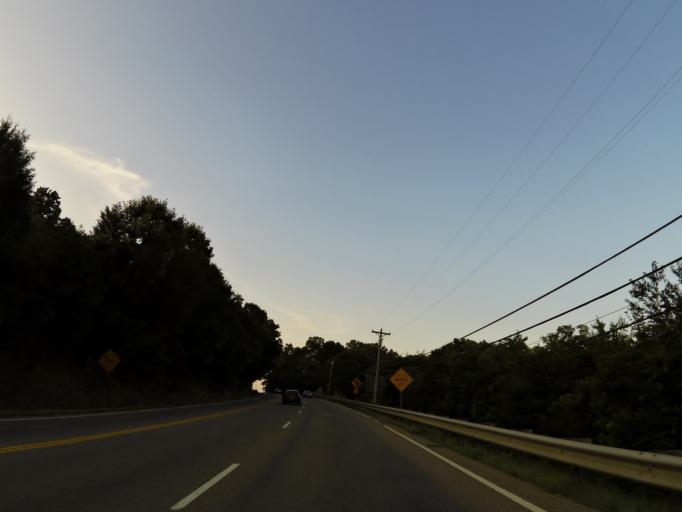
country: US
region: Tennessee
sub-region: Loudon County
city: Loudon
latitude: 35.7478
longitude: -84.3203
